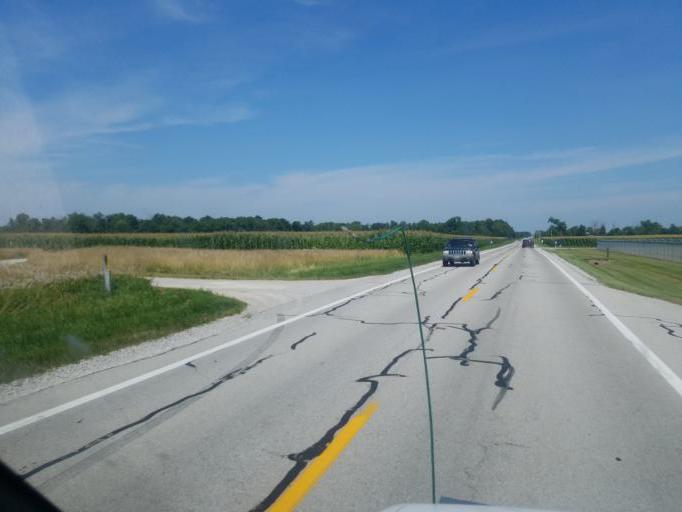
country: US
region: Ohio
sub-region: Shelby County
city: Botkins
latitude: 40.4961
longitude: -84.2855
